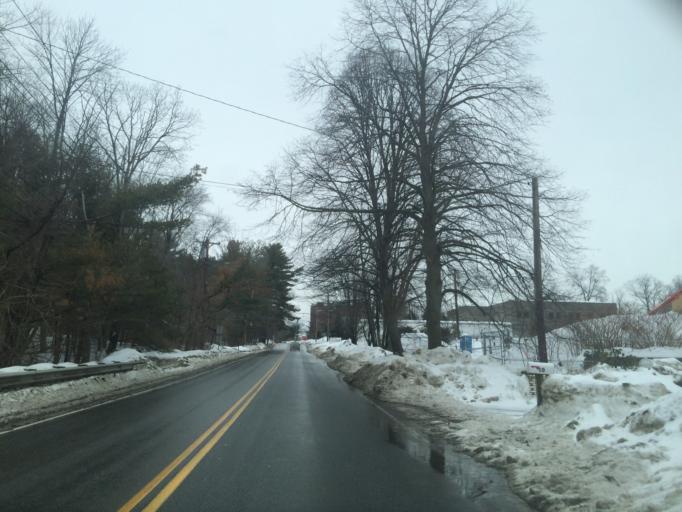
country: US
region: Massachusetts
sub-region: Middlesex County
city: Weston
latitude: 42.3791
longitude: -71.2752
